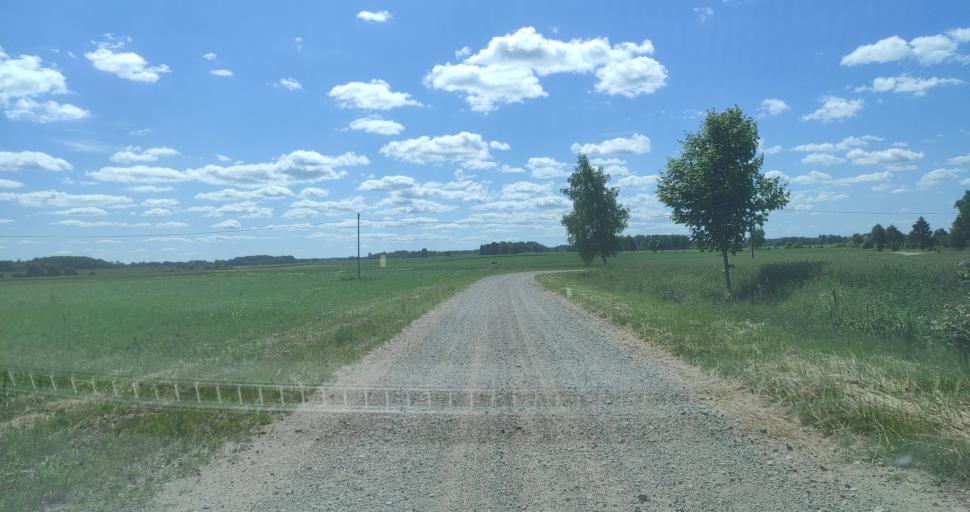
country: LV
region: Alsunga
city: Alsunga
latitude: 56.8686
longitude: 21.6974
